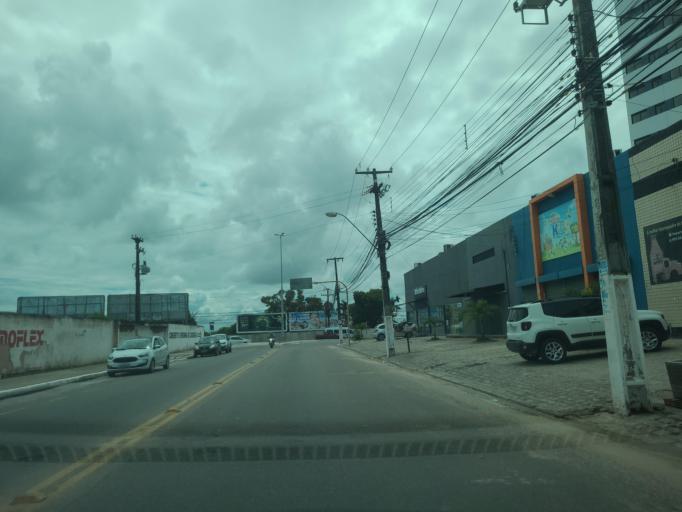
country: BR
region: Alagoas
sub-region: Maceio
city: Maceio
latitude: -9.6186
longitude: -35.7126
